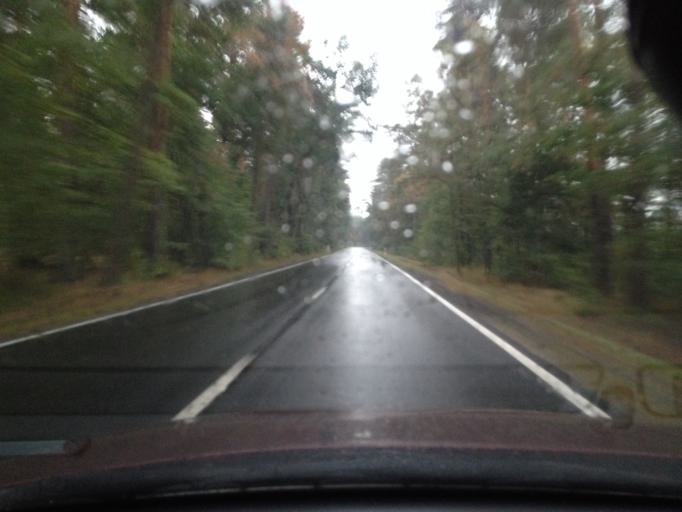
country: PL
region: Lubusz
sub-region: Powiat zaganski
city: Ilowa
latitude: 51.4434
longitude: 15.1972
